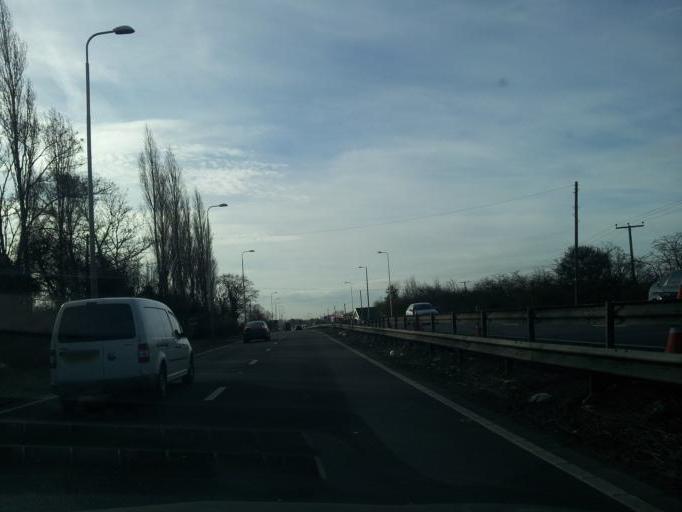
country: GB
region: England
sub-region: Central Bedfordshire
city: Tempsford
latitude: 52.1507
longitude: -0.3010
